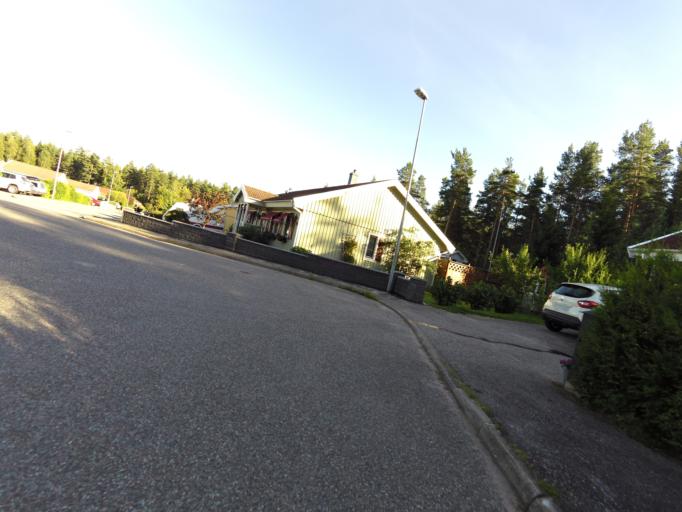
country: SE
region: Gaevleborg
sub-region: Gavle Kommun
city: Gavle
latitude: 60.6429
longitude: 17.1352
